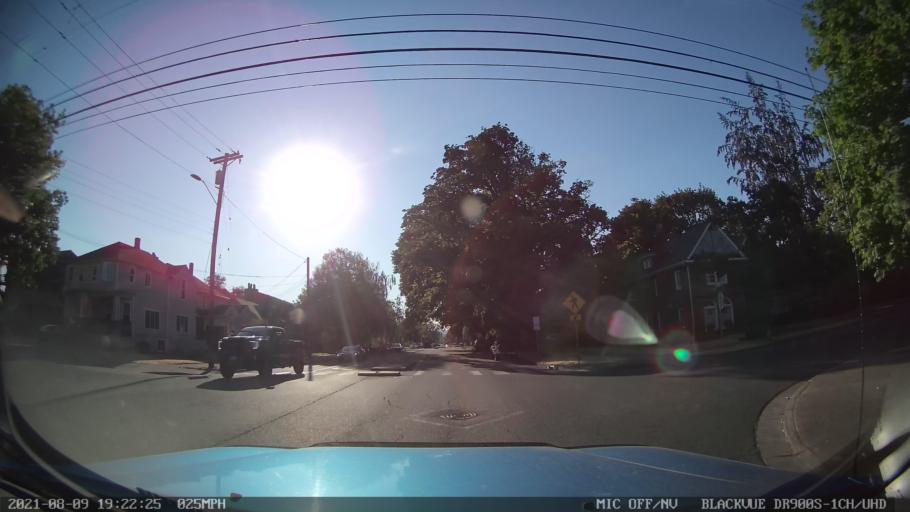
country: US
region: Oregon
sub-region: Marion County
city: Salem
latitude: 44.9395
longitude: -123.0225
